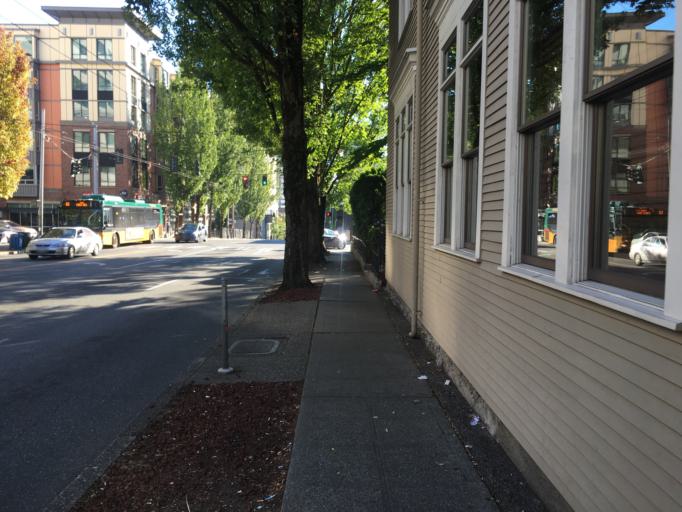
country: US
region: Washington
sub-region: King County
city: Seattle
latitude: 47.6097
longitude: -122.3246
